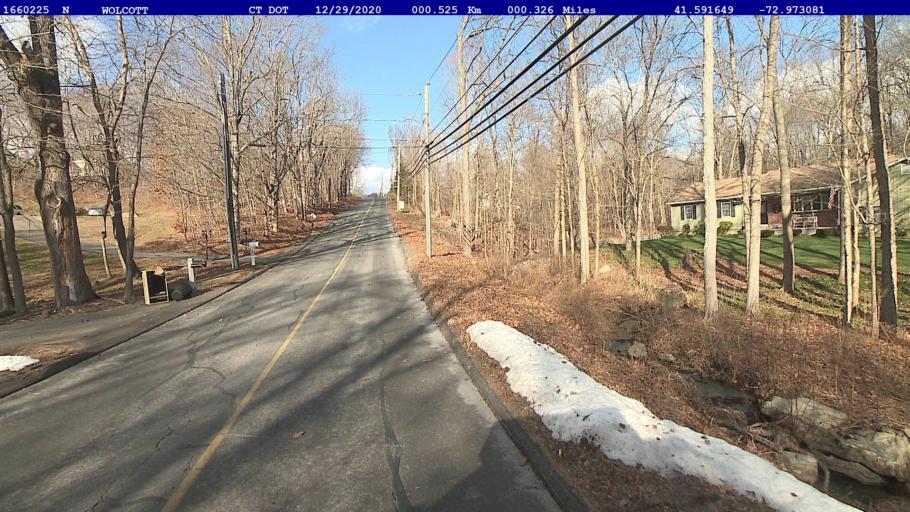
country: US
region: Connecticut
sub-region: New Haven County
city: Wolcott
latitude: 41.5918
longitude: -72.9731
